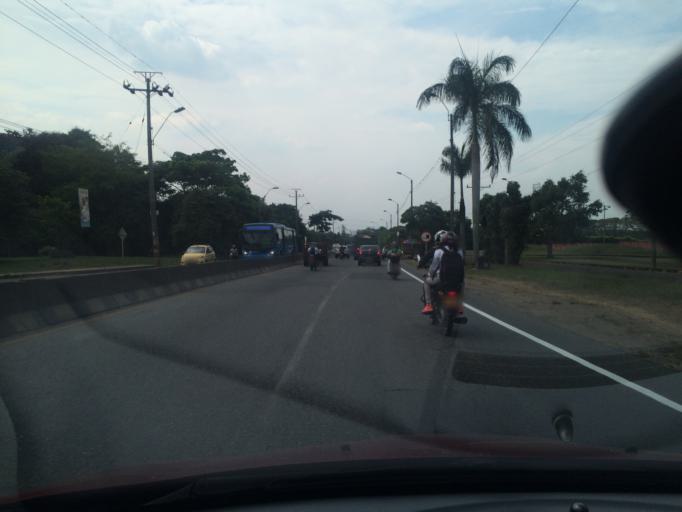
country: CO
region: Valle del Cauca
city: Jamundi
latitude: 3.3471
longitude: -76.5241
